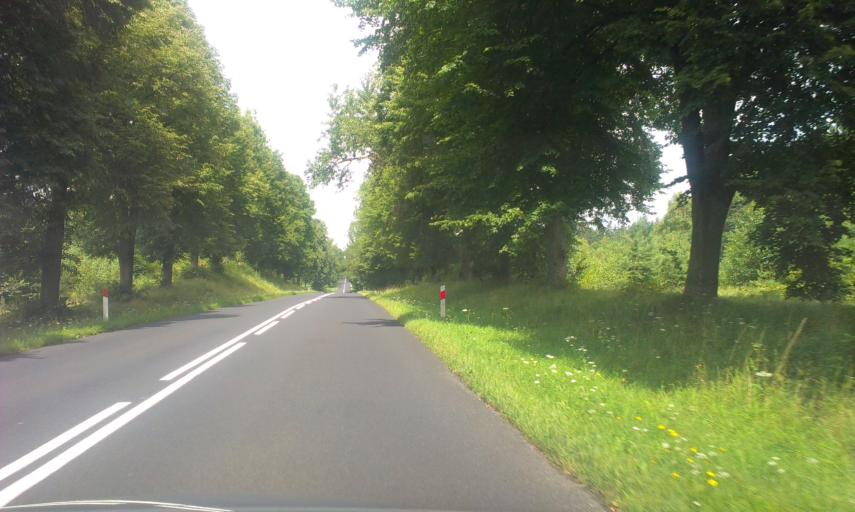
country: PL
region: West Pomeranian Voivodeship
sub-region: Powiat bialogardzki
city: Bialogard
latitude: 53.9295
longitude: 16.0630
